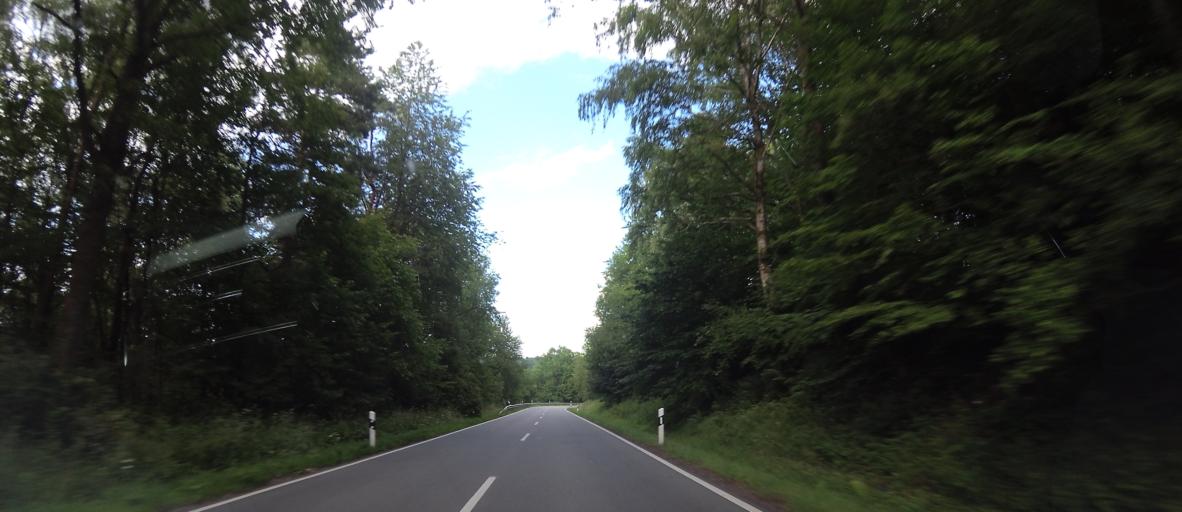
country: DE
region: Rheinland-Pfalz
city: Obersimten
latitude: 49.1720
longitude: 7.5817
